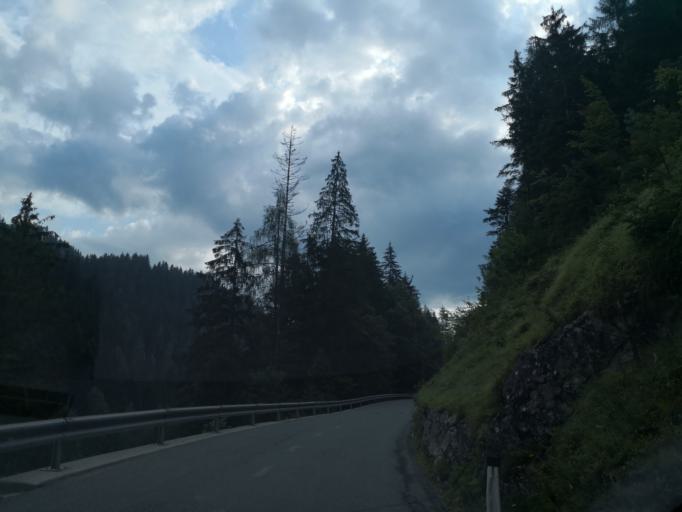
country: SI
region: Jezersko
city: Zgornje Jezersko
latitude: 46.3895
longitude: 14.4853
